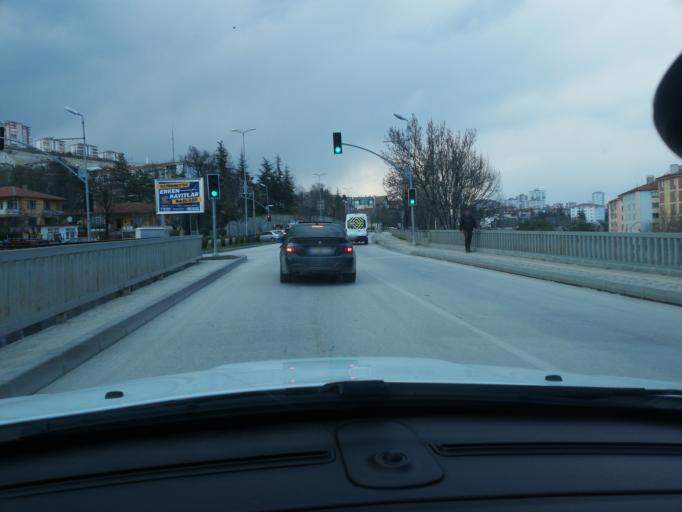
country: TR
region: Kastamonu
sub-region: Cide
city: Kastamonu
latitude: 41.3975
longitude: 33.7812
